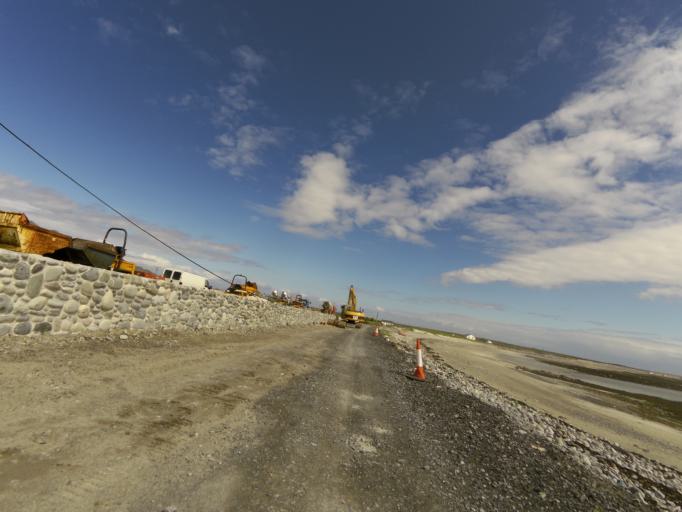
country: IE
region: Connaught
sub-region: County Galway
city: Oughterard
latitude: 53.1245
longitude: -9.6622
